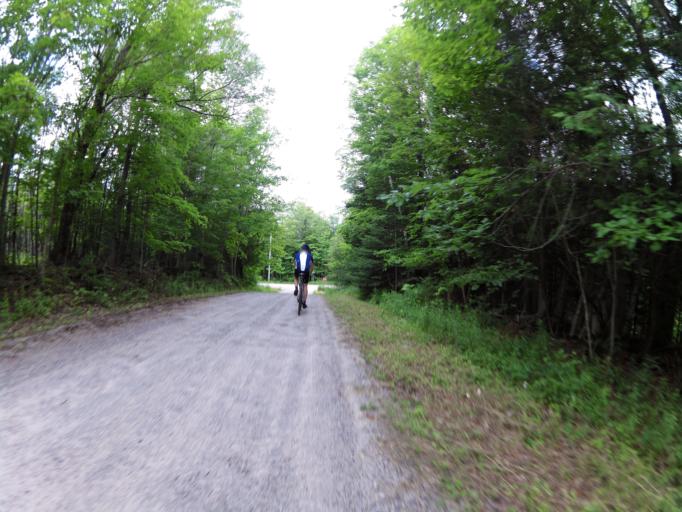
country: CA
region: Ontario
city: Perth
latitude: 45.0579
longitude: -76.4860
